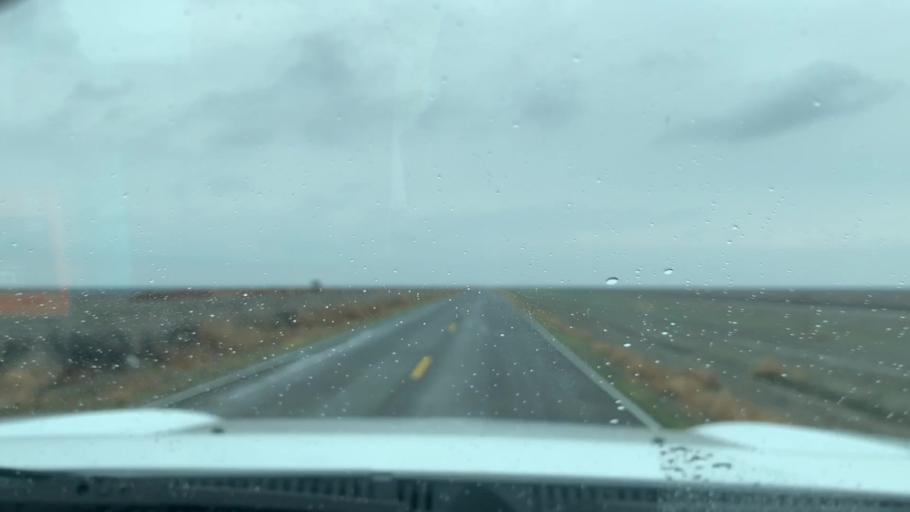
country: US
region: California
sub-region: Tulare County
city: Alpaugh
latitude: 35.9340
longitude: -119.6755
